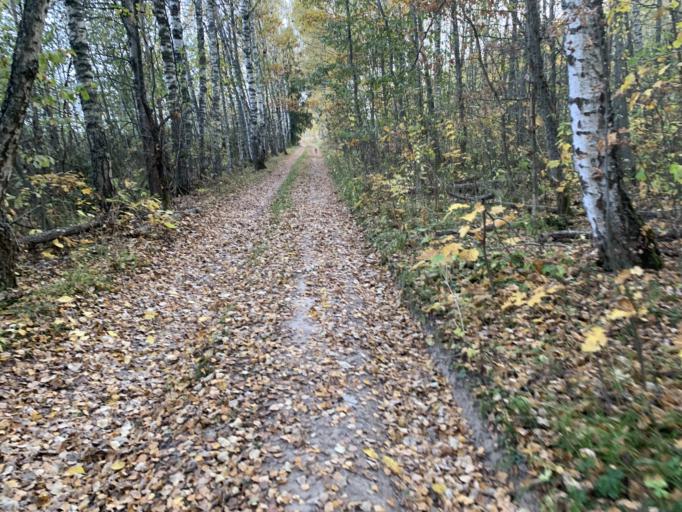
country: RU
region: Jaroslavl
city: Porech'ye-Rybnoye
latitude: 56.9859
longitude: 39.3803
